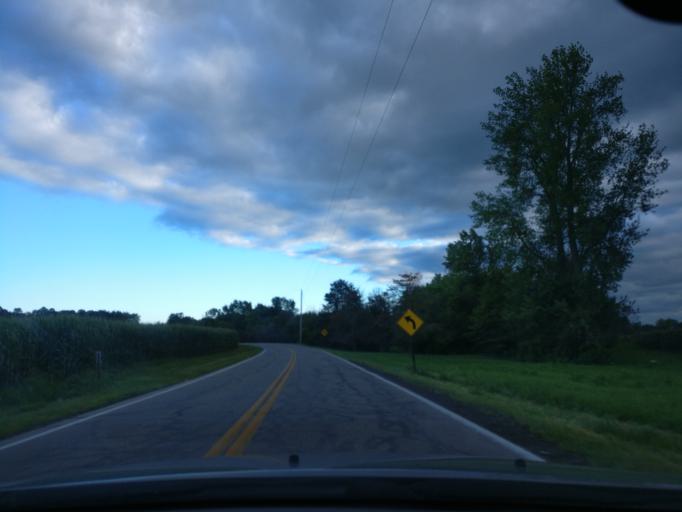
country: US
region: Ohio
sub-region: Greene County
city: Shawnee Hills
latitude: 39.6635
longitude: -83.7637
